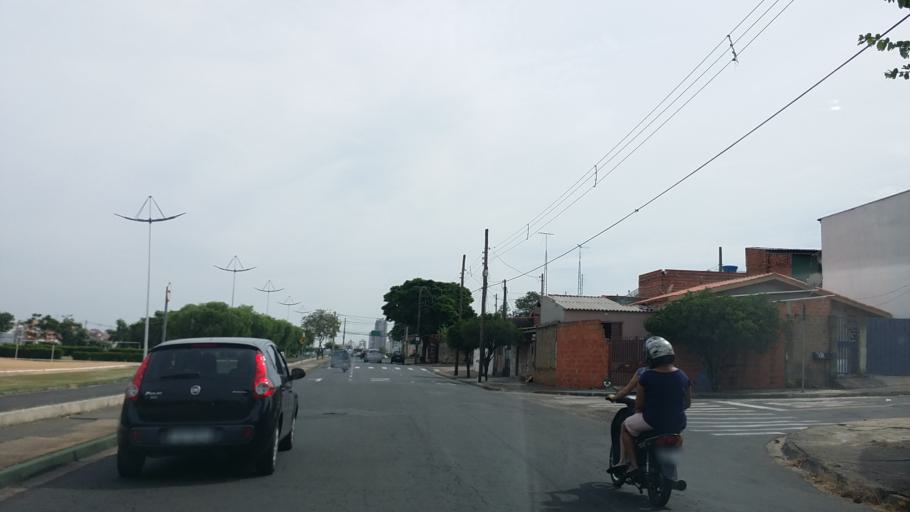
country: BR
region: Sao Paulo
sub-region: Indaiatuba
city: Indaiatuba
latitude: -23.1121
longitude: -47.2306
